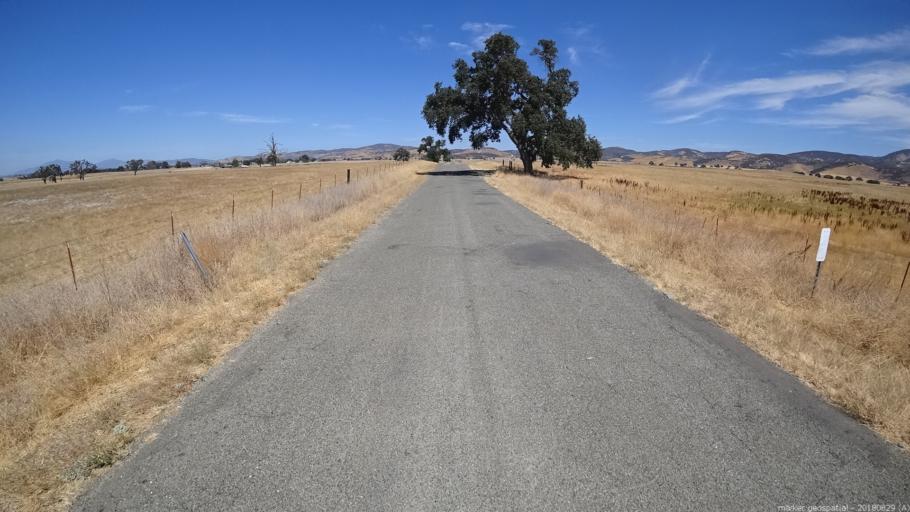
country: US
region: California
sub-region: San Luis Obispo County
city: Lake Nacimiento
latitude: 35.9267
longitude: -121.0643
